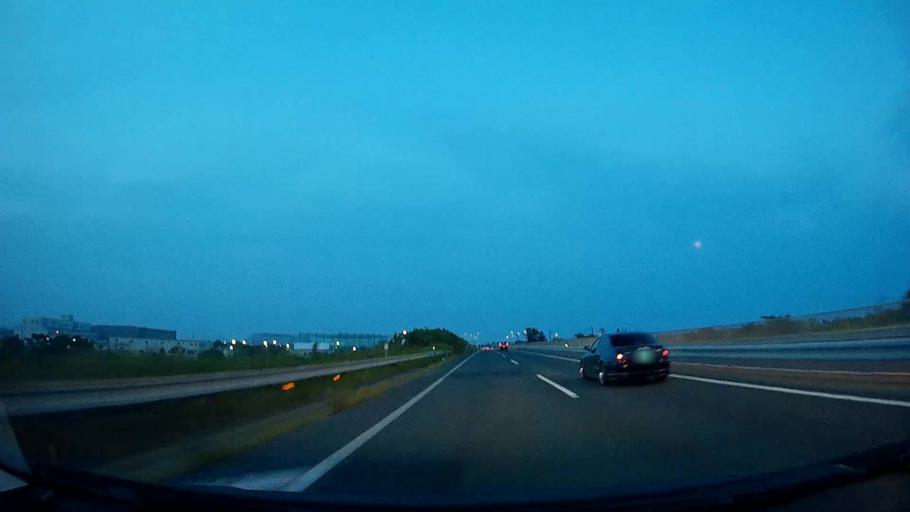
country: JP
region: Shizuoka
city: Hamamatsu
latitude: 34.6763
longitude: 137.6458
